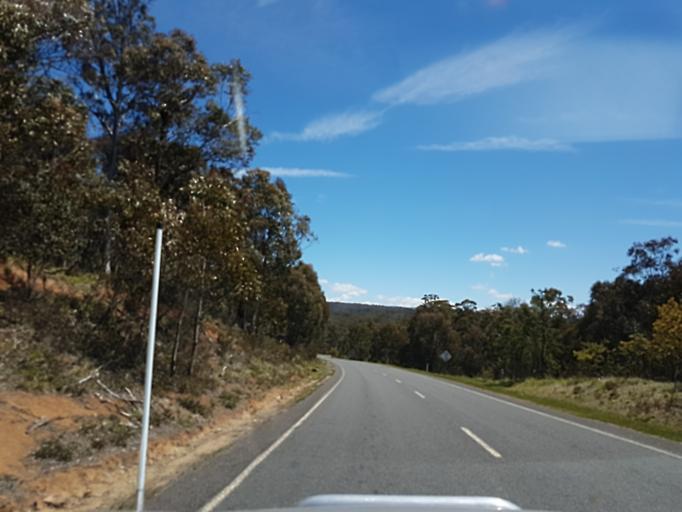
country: AU
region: Victoria
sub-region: Alpine
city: Mount Beauty
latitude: -37.0793
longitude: 147.3557
